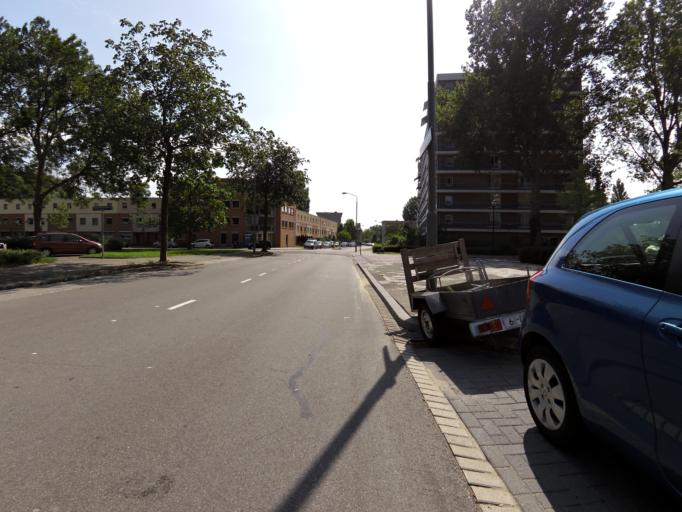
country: NL
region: South Holland
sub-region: Gemeente Dordrecht
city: Dordrecht
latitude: 51.7910
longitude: 4.6560
